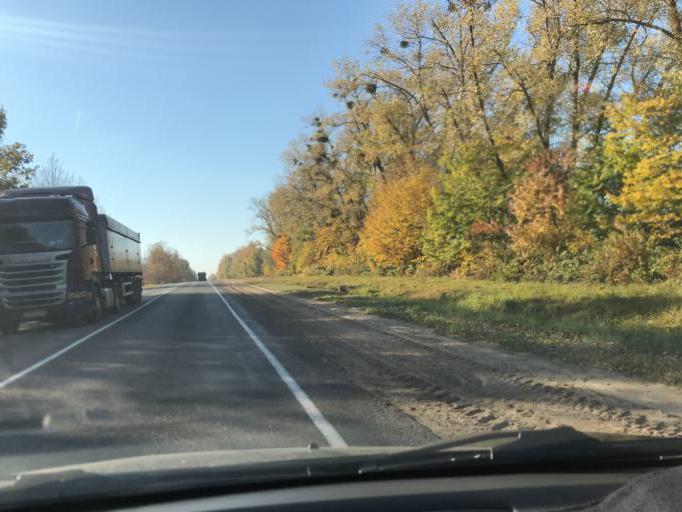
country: BY
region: Mogilev
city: Hlusha
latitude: 53.0922
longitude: 28.9278
